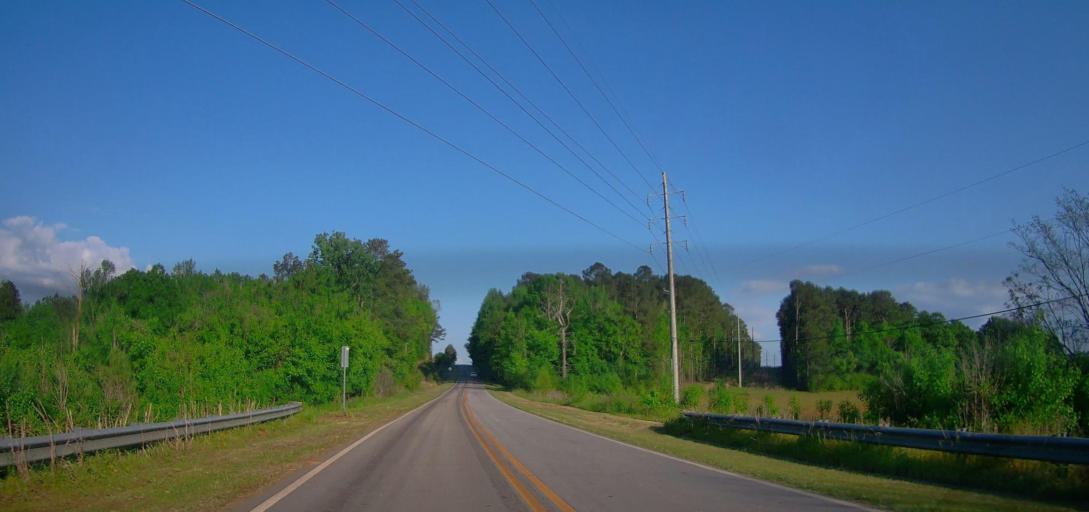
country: US
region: Georgia
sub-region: Putnam County
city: Eatonton
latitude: 33.3155
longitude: -83.3655
